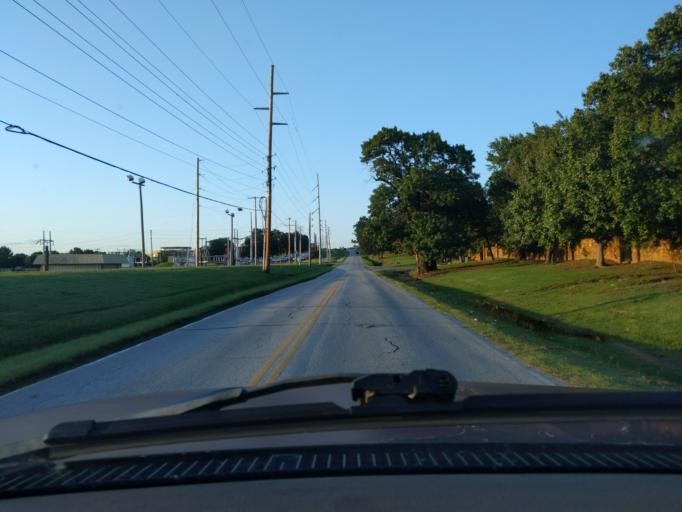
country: US
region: Oklahoma
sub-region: Tulsa County
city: Jenks
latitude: 36.0404
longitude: -95.9489
